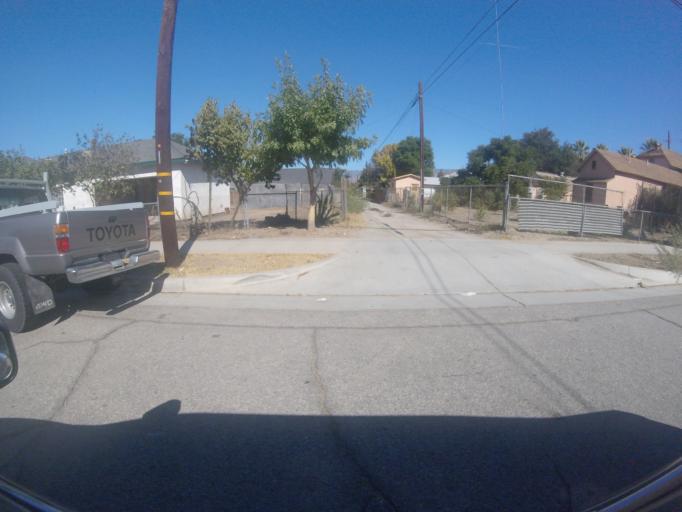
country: US
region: California
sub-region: San Bernardino County
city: Redlands
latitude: 34.0641
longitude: -117.1810
